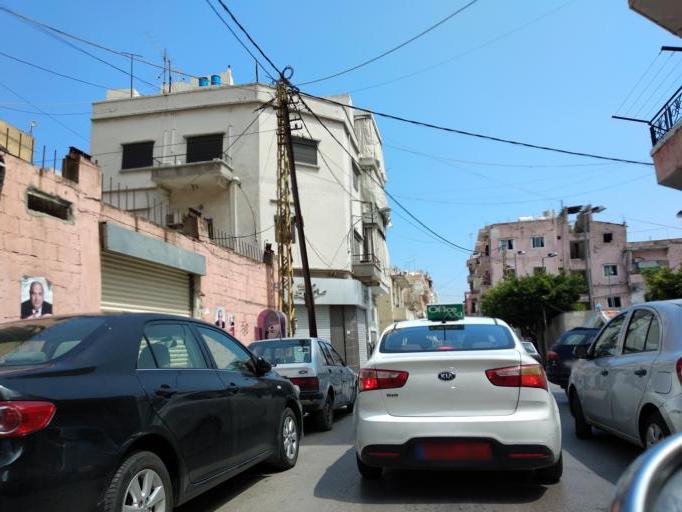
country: LB
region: Mont-Liban
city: Jdaidet el Matn
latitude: 33.8938
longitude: 35.5337
